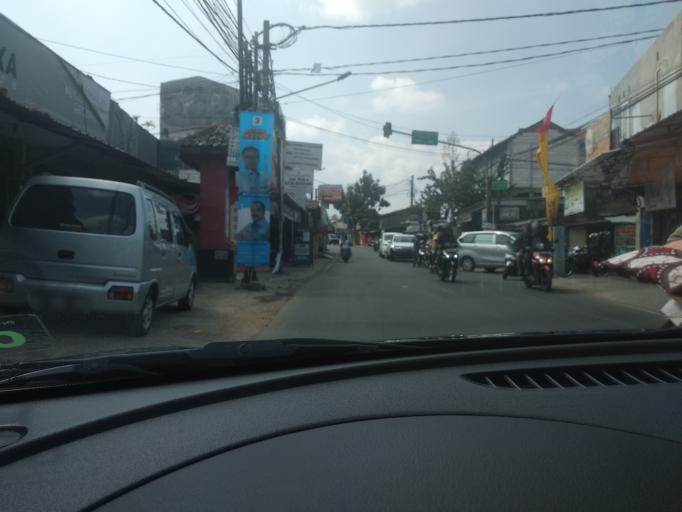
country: ID
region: West Java
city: Cimahi
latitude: -6.8914
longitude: 107.5630
